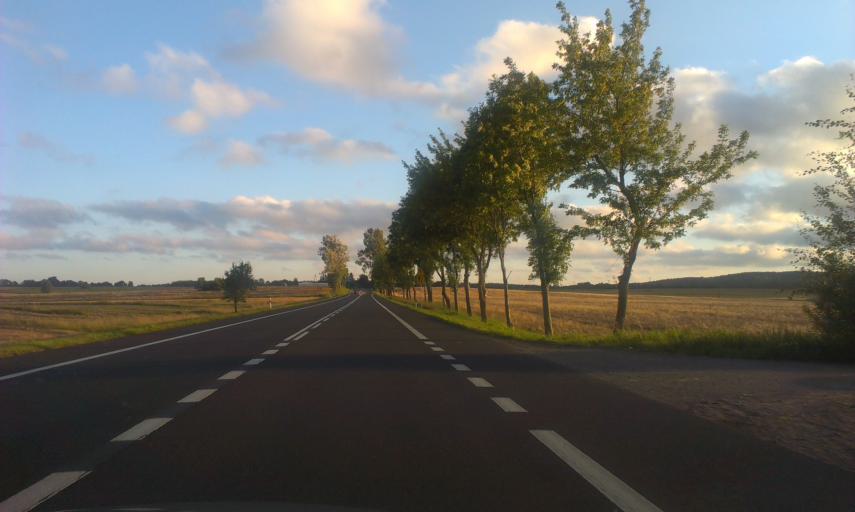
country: PL
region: West Pomeranian Voivodeship
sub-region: Powiat slawienski
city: Darlowo
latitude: 54.2876
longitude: 16.4909
